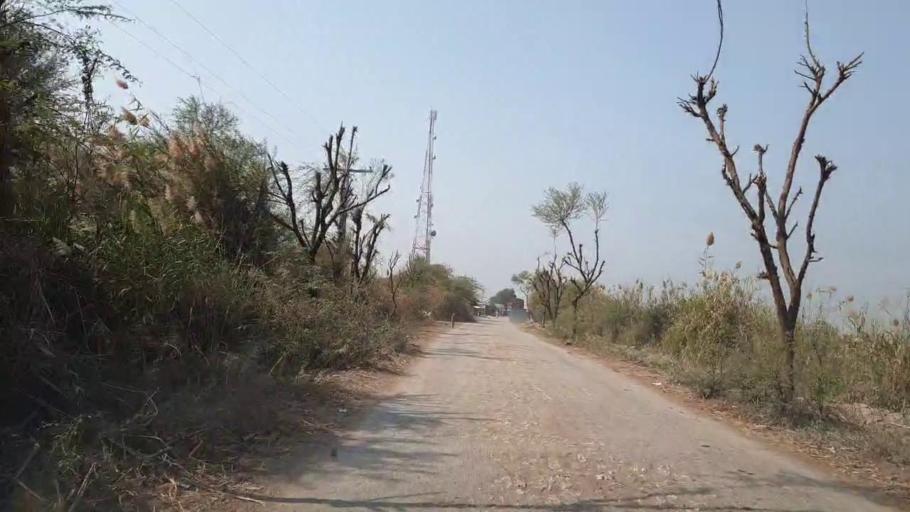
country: PK
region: Sindh
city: Mirpur Khas
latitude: 25.7076
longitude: 69.1310
